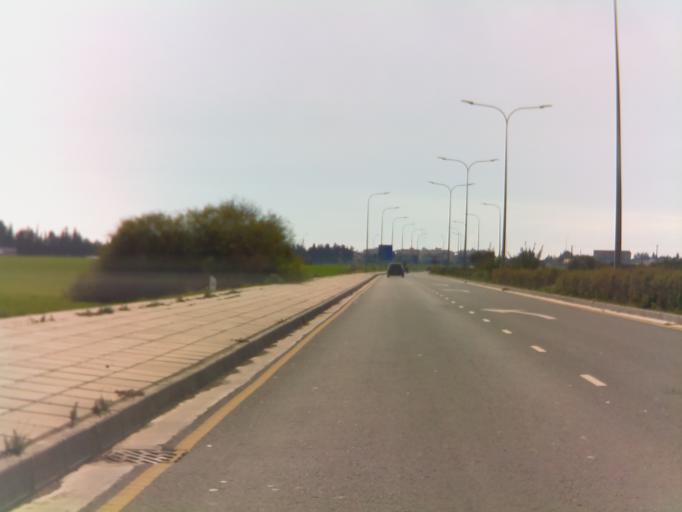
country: CY
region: Larnaka
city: Meneou
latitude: 34.8711
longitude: 33.5992
